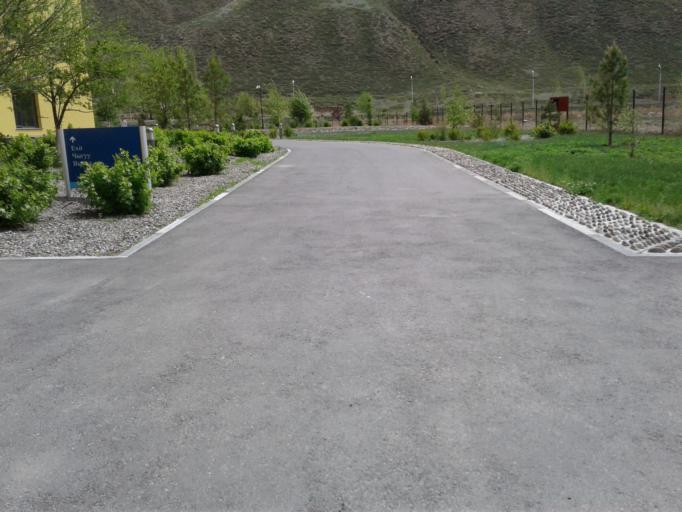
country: KG
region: Naryn
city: Naryn
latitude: 41.4296
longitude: 75.9002
